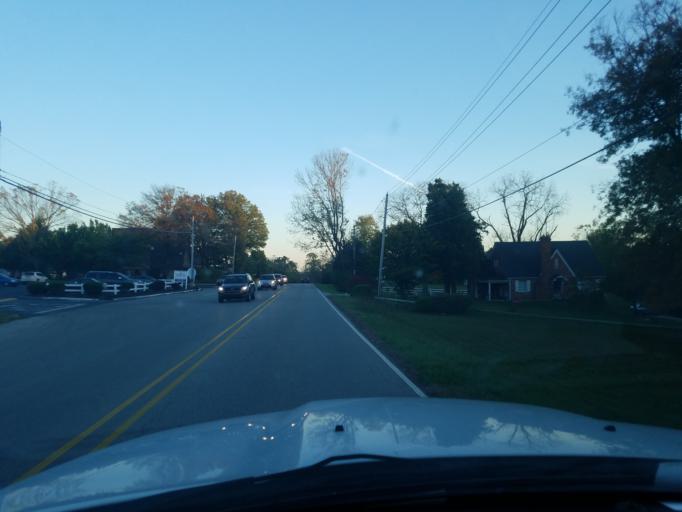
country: US
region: Indiana
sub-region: Floyd County
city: New Albany
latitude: 38.3151
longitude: -85.8525
